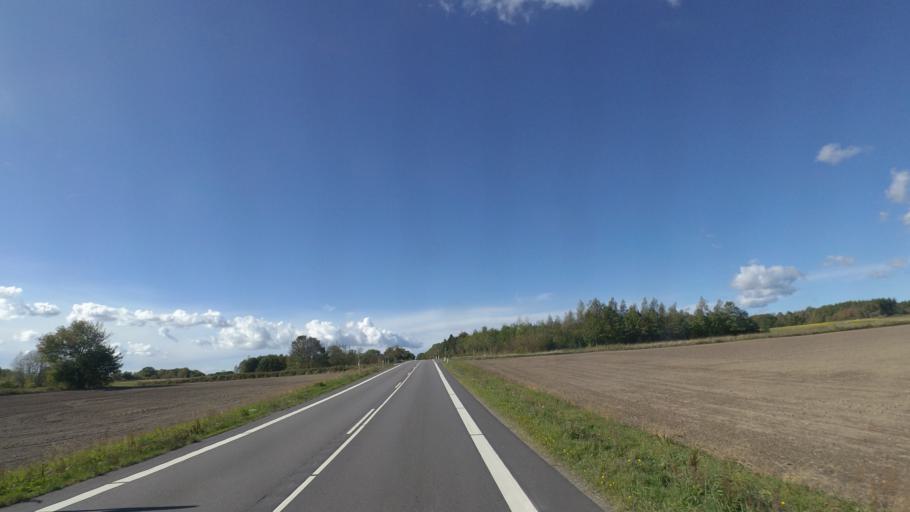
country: DK
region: Capital Region
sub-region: Bornholm Kommune
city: Akirkeby
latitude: 55.0671
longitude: 15.0005
